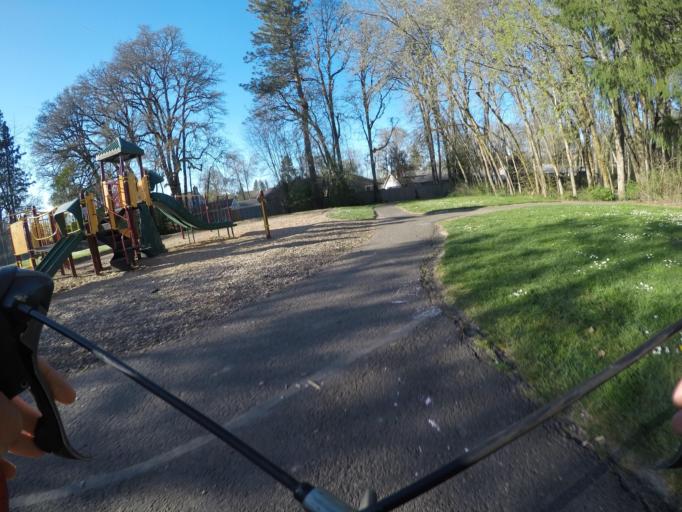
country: US
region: Oregon
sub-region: Washington County
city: Aloha
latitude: 45.4983
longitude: -122.8629
